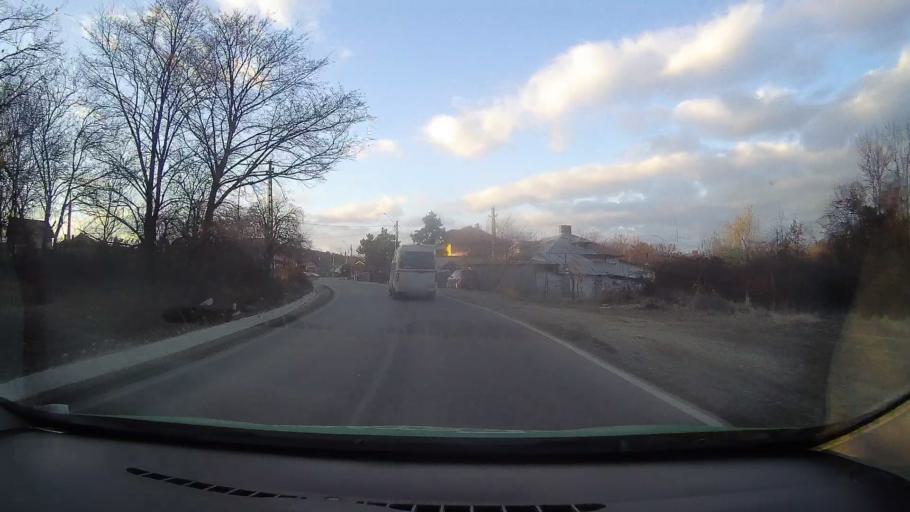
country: RO
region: Dambovita
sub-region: Comuna Gura Ocnitei
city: Gura Ocnitei
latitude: 44.9630
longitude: 25.6010
